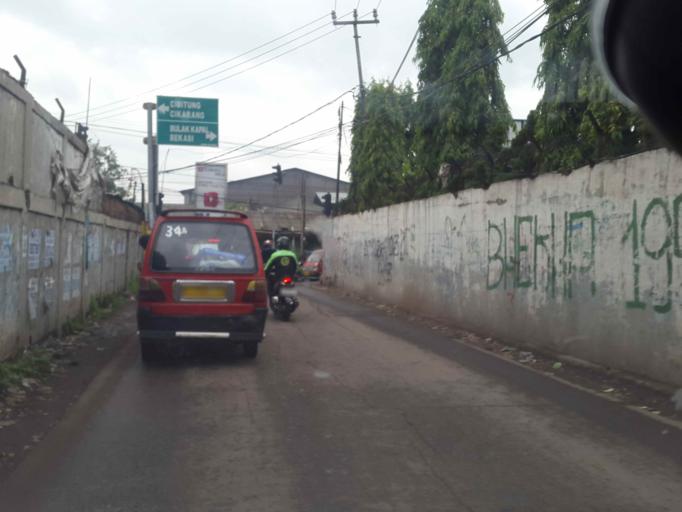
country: ID
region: West Java
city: Bekasi
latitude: -6.2572
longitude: 107.0409
